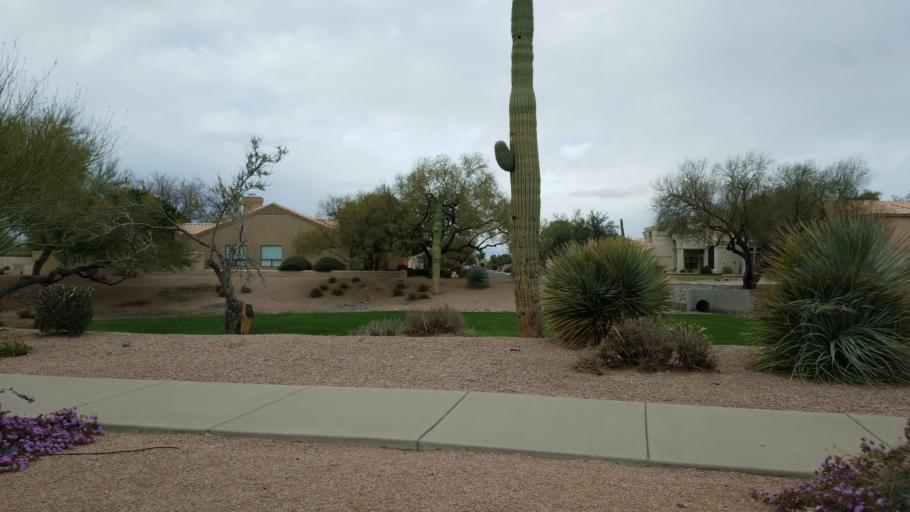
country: US
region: Arizona
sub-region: Maricopa County
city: Paradise Valley
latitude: 33.6189
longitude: -111.8862
